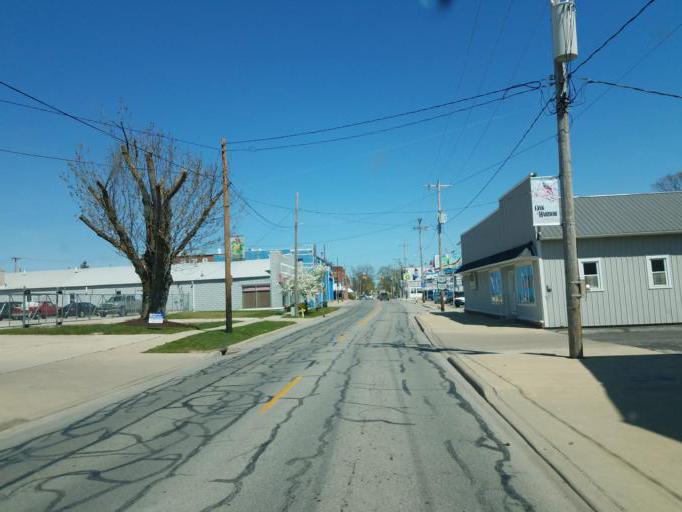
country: US
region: Ohio
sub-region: Ottawa County
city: Oak Harbor
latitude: 41.5062
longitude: -83.1450
